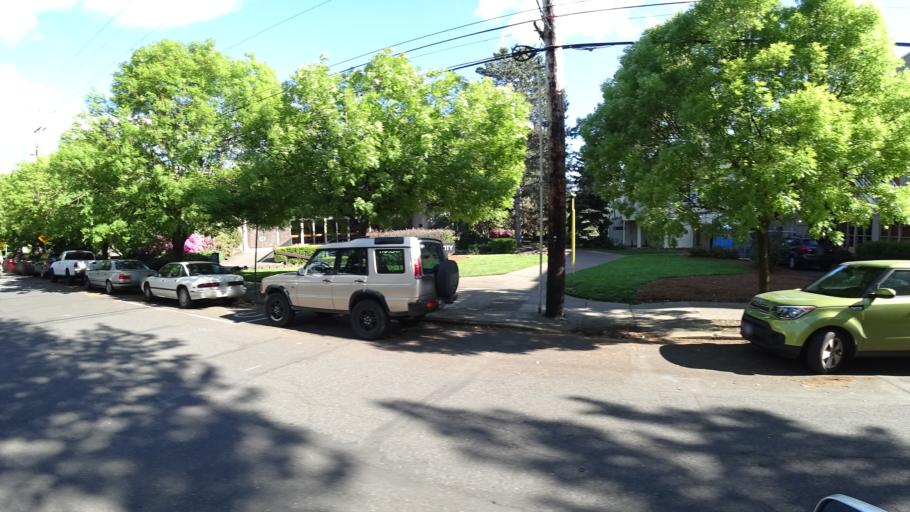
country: US
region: Oregon
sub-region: Multnomah County
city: Portland
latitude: 45.5222
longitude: -122.6516
